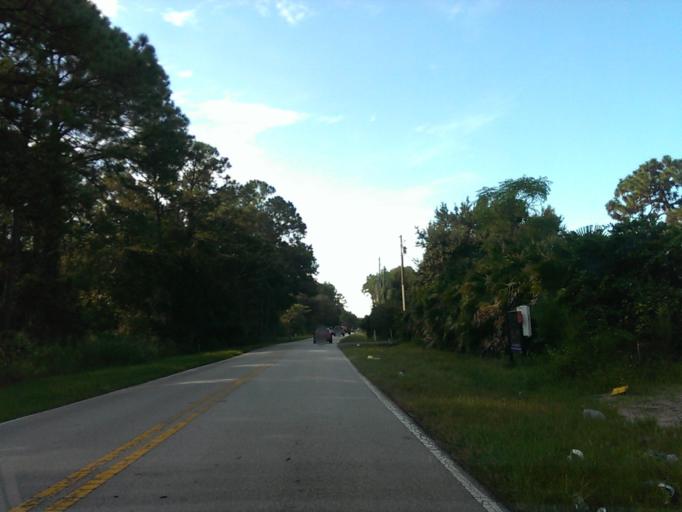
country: US
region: Florida
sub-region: Orange County
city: Lake Butler
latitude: 28.4559
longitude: -81.5961
